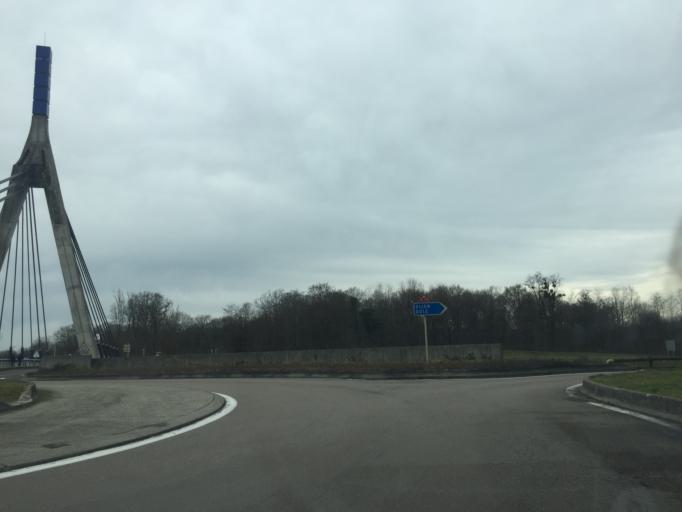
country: FR
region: Franche-Comte
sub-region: Departement du Jura
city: Bletterans
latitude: 46.7766
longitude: 5.5226
